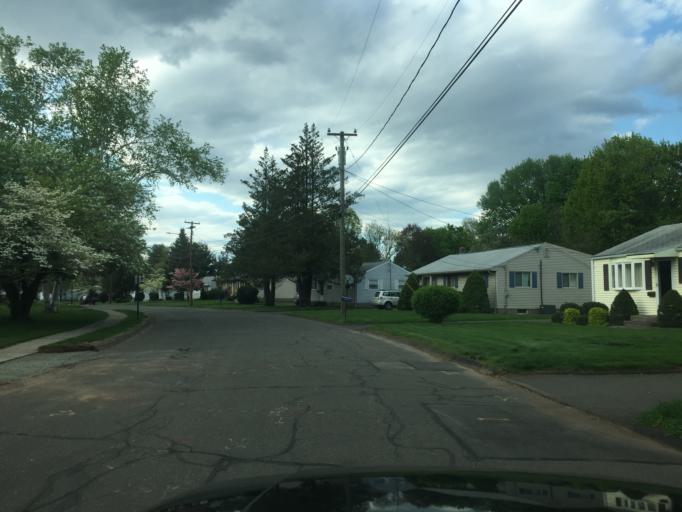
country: US
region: Connecticut
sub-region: Hartford County
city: Kensington
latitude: 41.6234
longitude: -72.7507
